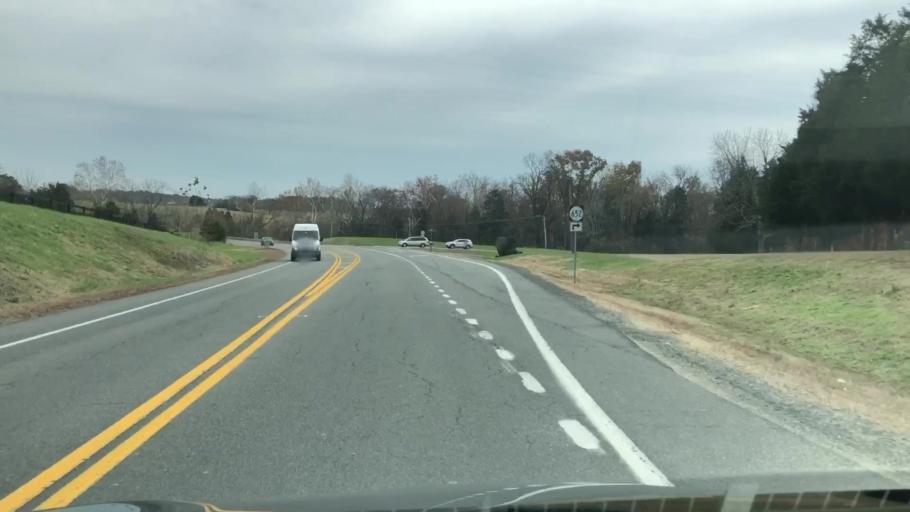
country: US
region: Virginia
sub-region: Fauquier County
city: New Baltimore
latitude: 38.7570
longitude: -77.6764
